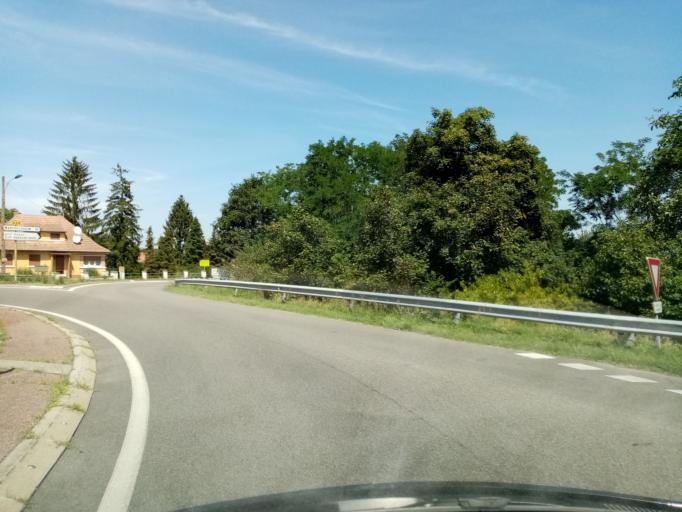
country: FR
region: Alsace
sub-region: Departement du Haut-Rhin
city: Neuf-Brisach
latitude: 48.0234
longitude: 7.5347
